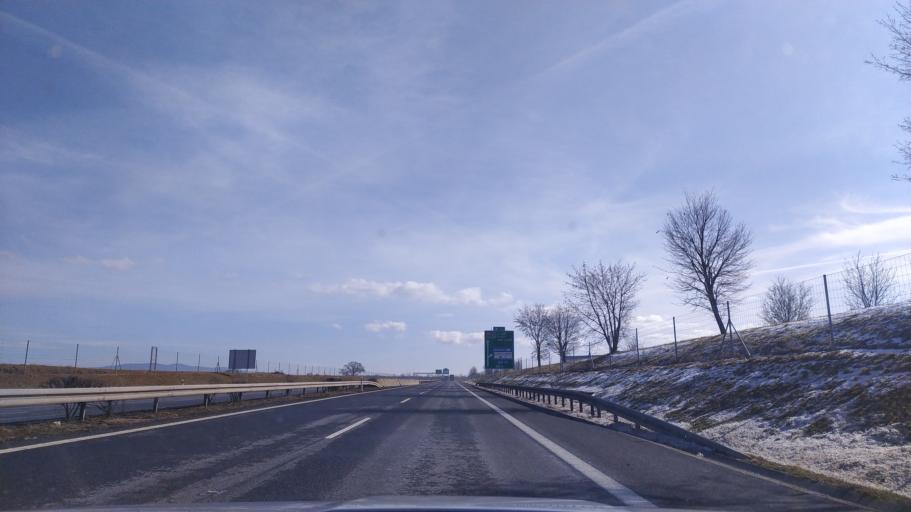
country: CZ
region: Karlovarsky
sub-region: Okres Cheb
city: Cheb
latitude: 50.0934
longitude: 12.4121
